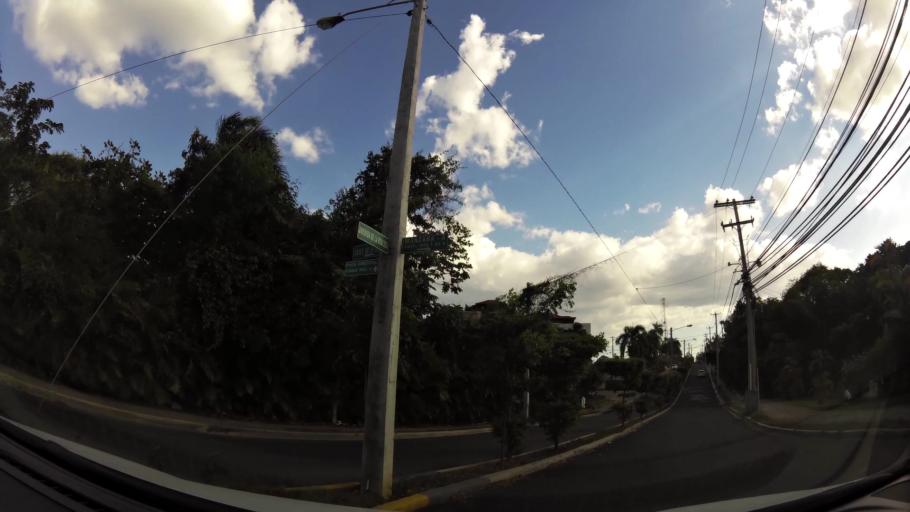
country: DO
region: Nacional
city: Santo Domingo
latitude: 18.5099
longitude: -69.9835
